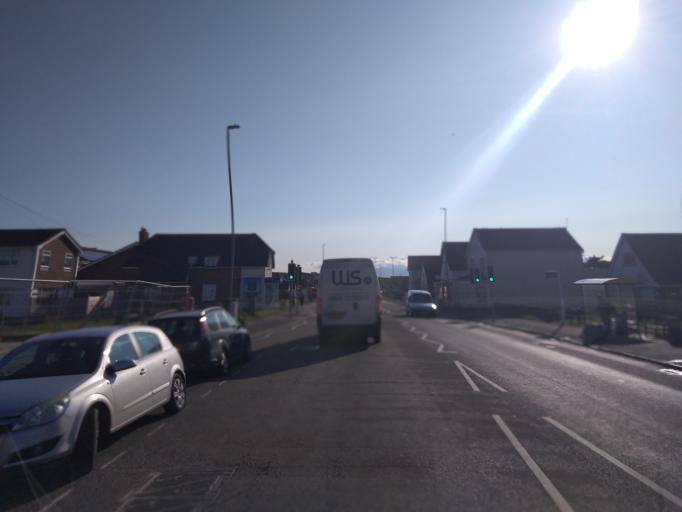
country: GB
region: England
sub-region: East Sussex
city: Peacehaven
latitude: 50.7902
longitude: 0.0069
